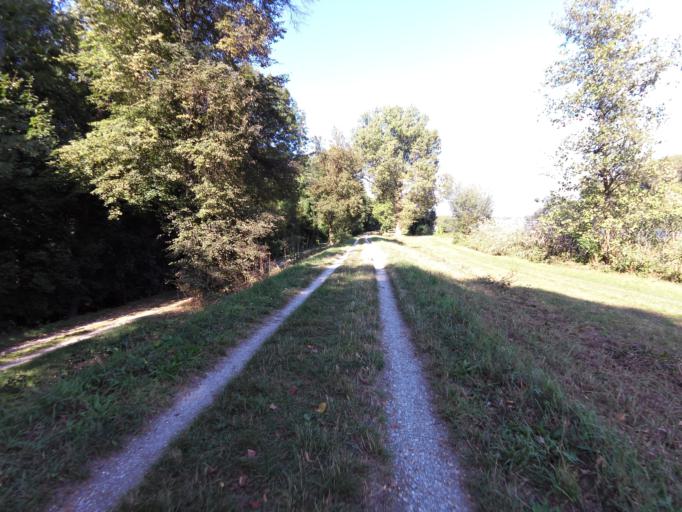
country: DE
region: Bavaria
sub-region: Lower Bavaria
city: Ergolding
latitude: 48.5625
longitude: 12.1829
